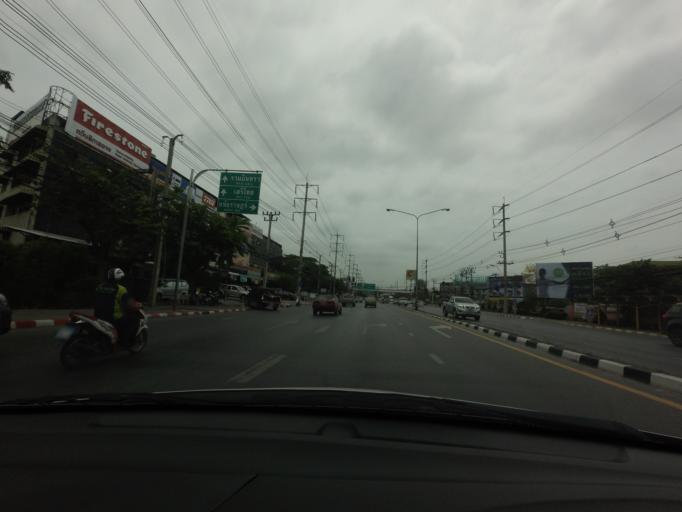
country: TH
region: Bangkok
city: Min Buri
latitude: 13.8172
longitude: 100.7228
